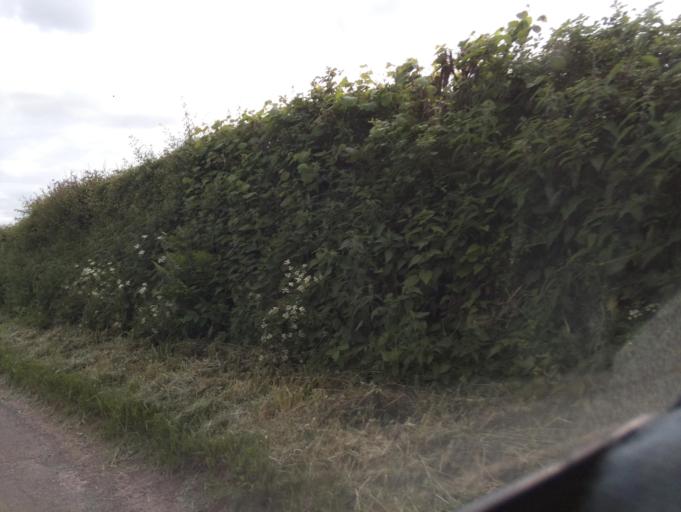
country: GB
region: England
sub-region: Herefordshire
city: Evesbatch
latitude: 52.0975
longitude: -2.4306
